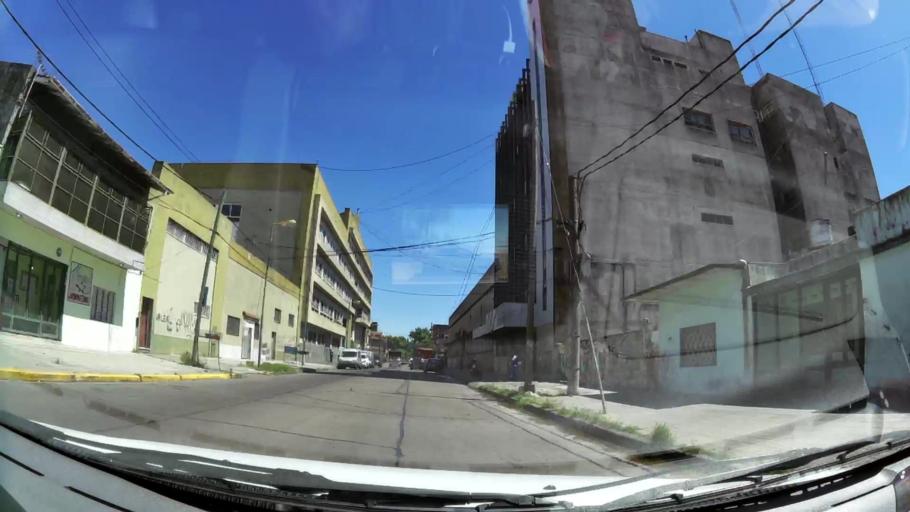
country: AR
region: Buenos Aires
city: Caseros
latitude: -34.5840
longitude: -58.5556
